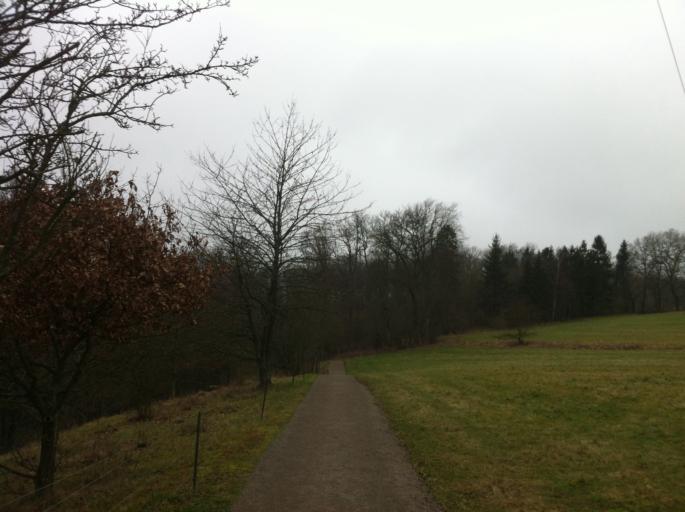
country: SE
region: Skane
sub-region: Helsingborg
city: Gantofta
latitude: 55.9984
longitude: 12.7901
